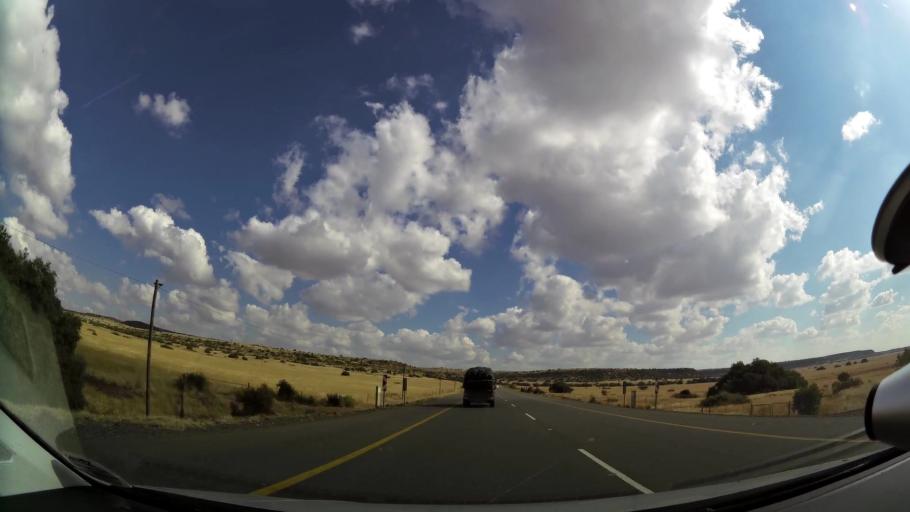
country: ZA
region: Orange Free State
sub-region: Mangaung Metropolitan Municipality
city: Bloemfontein
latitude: -29.1476
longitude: 26.0711
